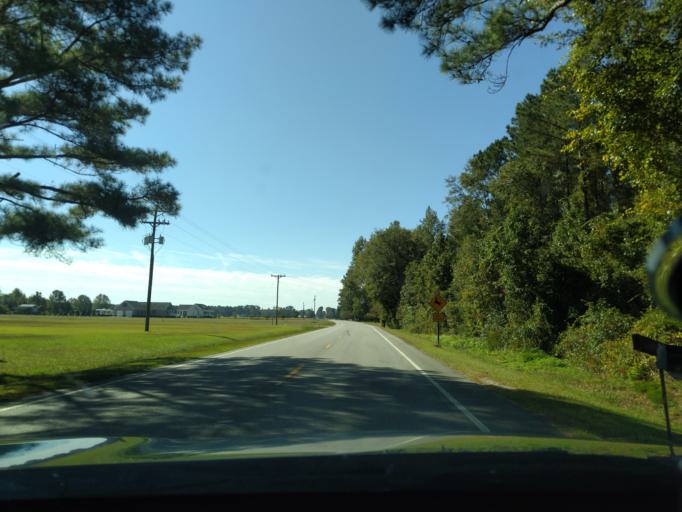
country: US
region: North Carolina
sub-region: Washington County
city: Plymouth
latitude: 35.7046
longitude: -76.7640
